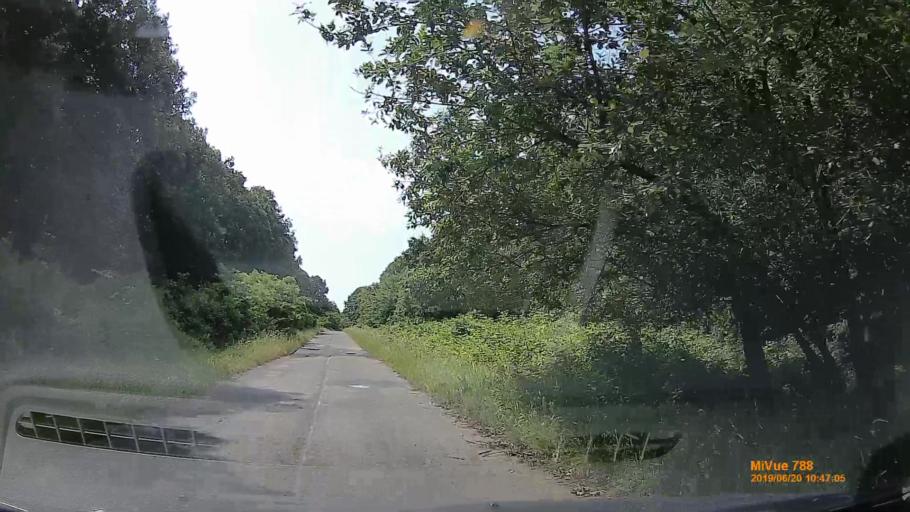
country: HU
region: Baranya
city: Hidas
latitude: 46.1774
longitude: 18.5818
